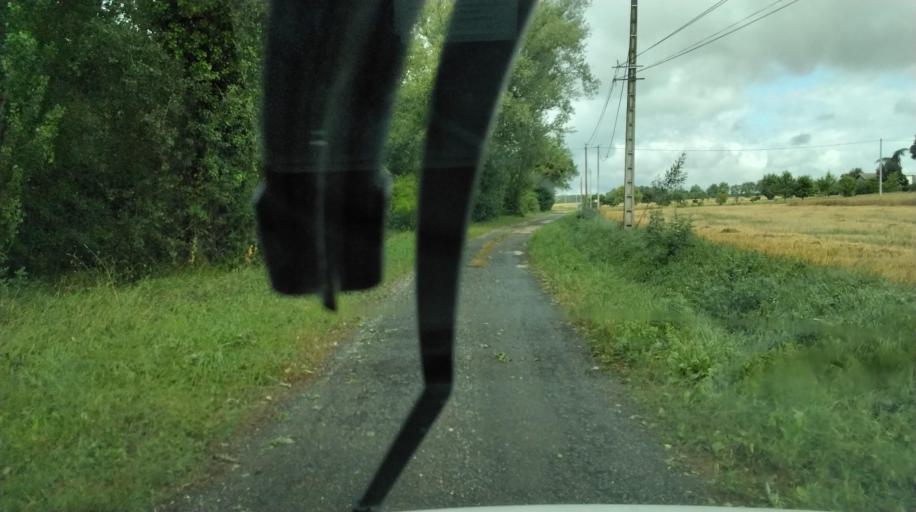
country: FR
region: Midi-Pyrenees
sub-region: Departement de la Haute-Garonne
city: Rieumes
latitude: 43.4226
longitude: 1.1561
